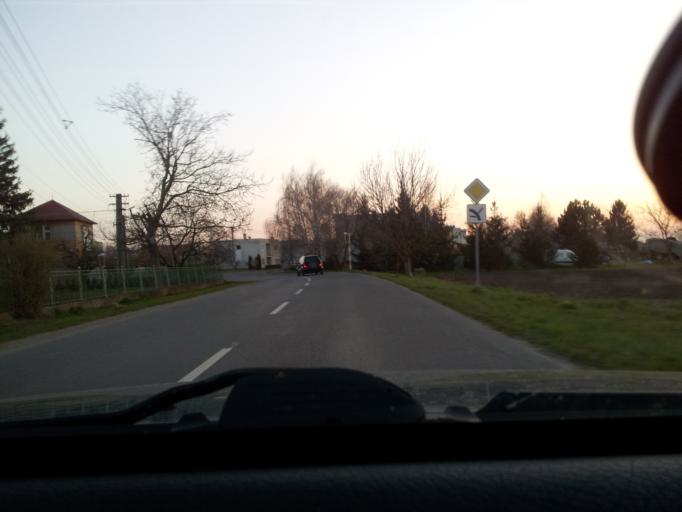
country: SK
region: Nitriansky
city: Levice
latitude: 48.2449
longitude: 18.5768
